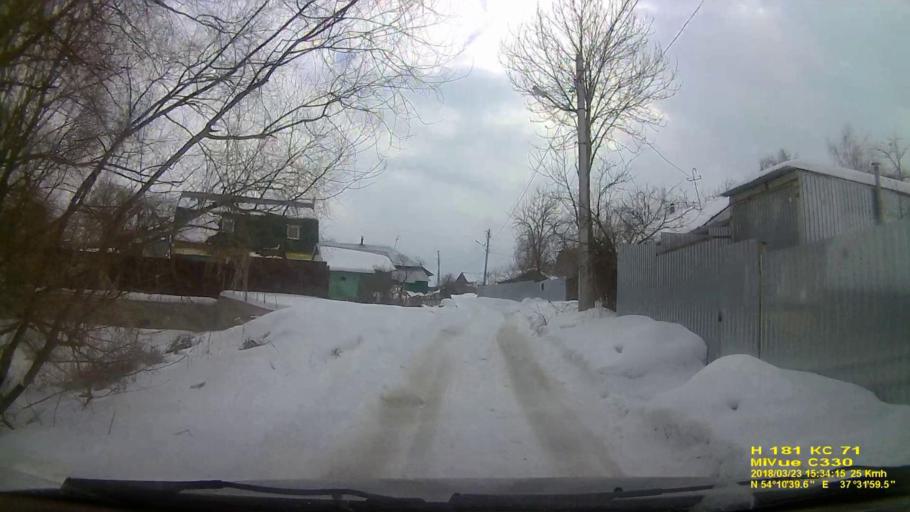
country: RU
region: Tula
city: Kosaya Gora
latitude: 54.1775
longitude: 37.5331
